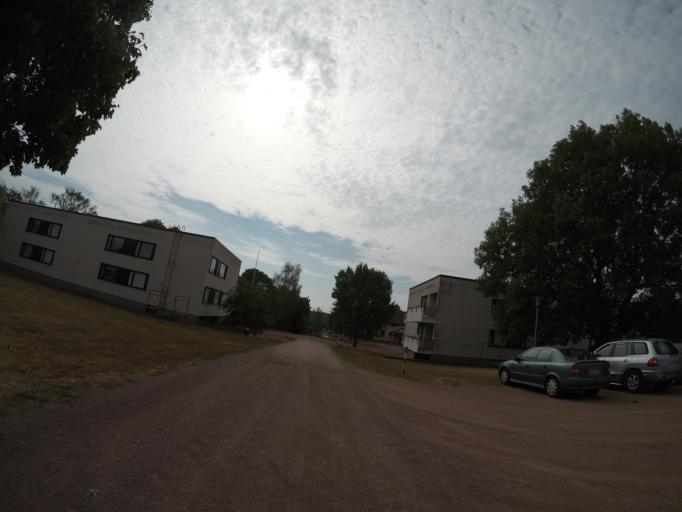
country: AX
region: Alands landsbygd
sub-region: Finstroem
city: Finstroem
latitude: 60.2334
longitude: 19.9907
